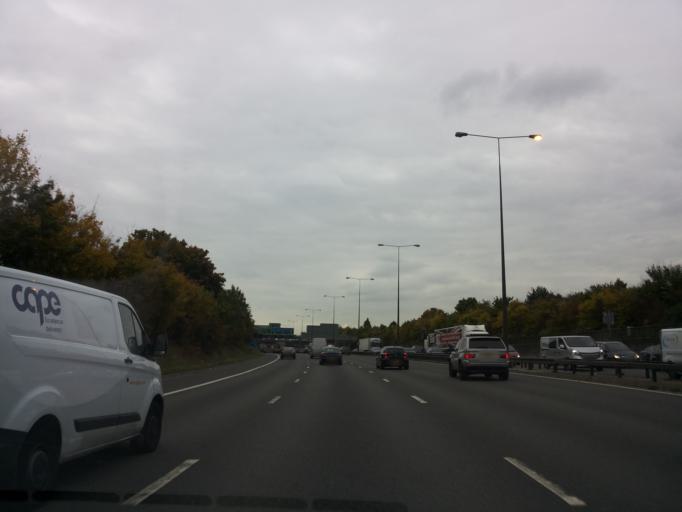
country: GB
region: England
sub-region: Kent
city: Dartford
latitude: 51.4460
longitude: 0.2357
